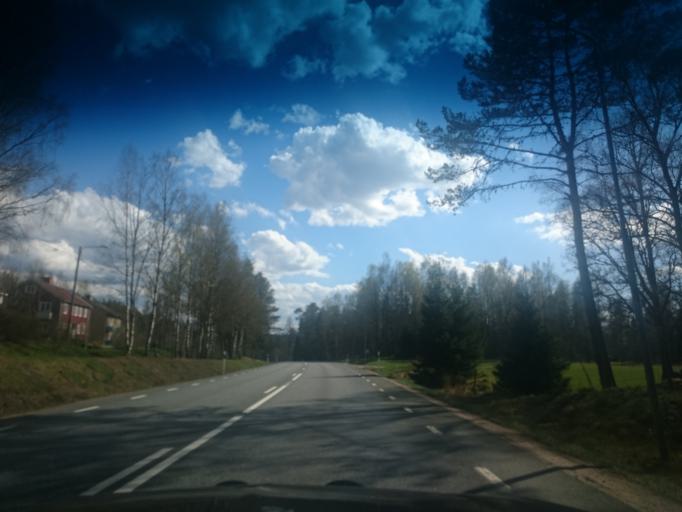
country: SE
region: Kronoberg
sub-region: Vaxjo Kommun
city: Braas
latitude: 57.2268
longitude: 15.1444
